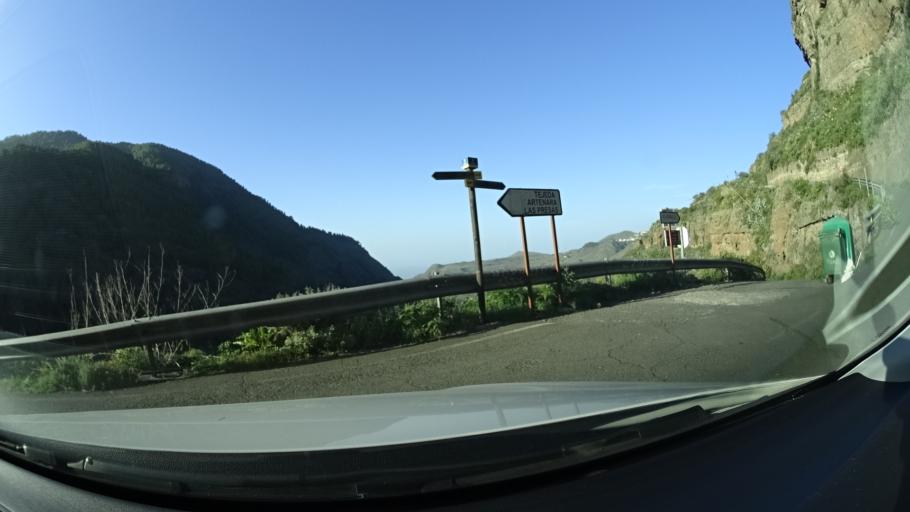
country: ES
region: Canary Islands
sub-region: Provincia de Las Palmas
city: Artenara
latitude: 28.0498
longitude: -15.6661
